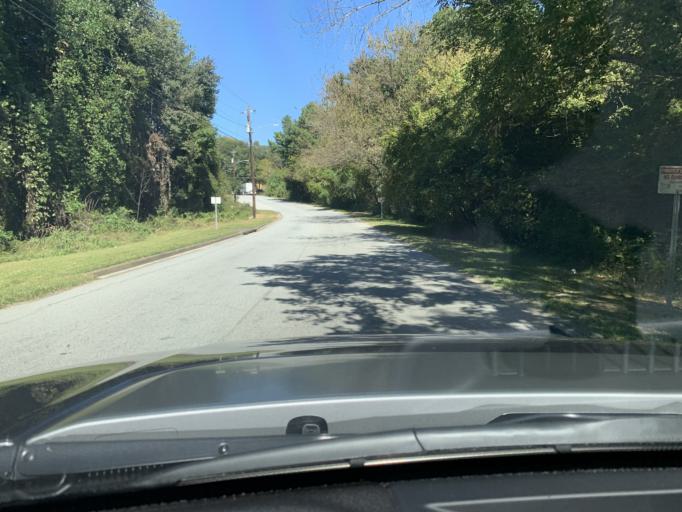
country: US
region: Georgia
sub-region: Clayton County
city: Conley
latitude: 33.6648
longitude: -84.3275
